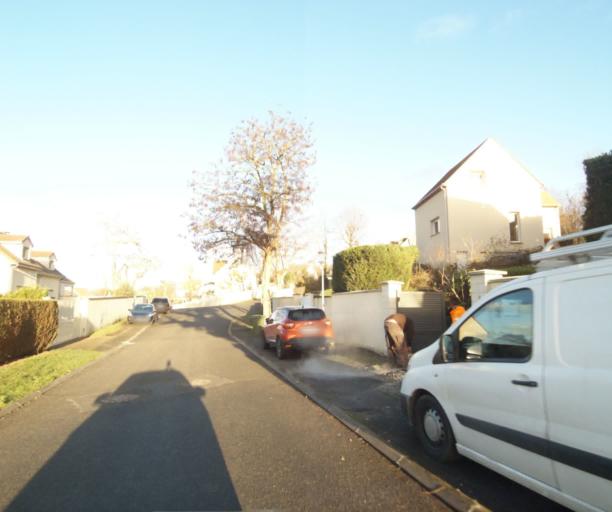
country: FR
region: Ile-de-France
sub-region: Departement des Yvelines
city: Meulan-en-Yvelines
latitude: 49.0136
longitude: 1.9162
